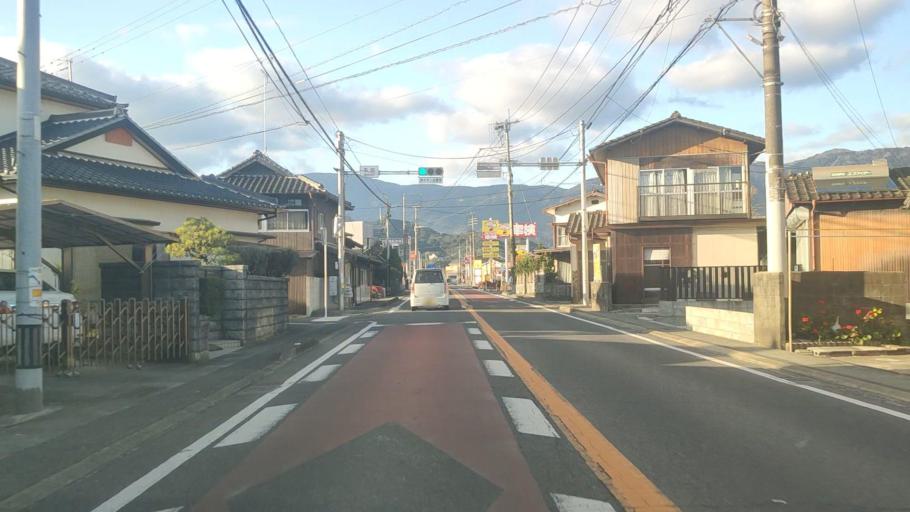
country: JP
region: Saga Prefecture
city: Saga-shi
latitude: 33.2902
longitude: 130.2047
